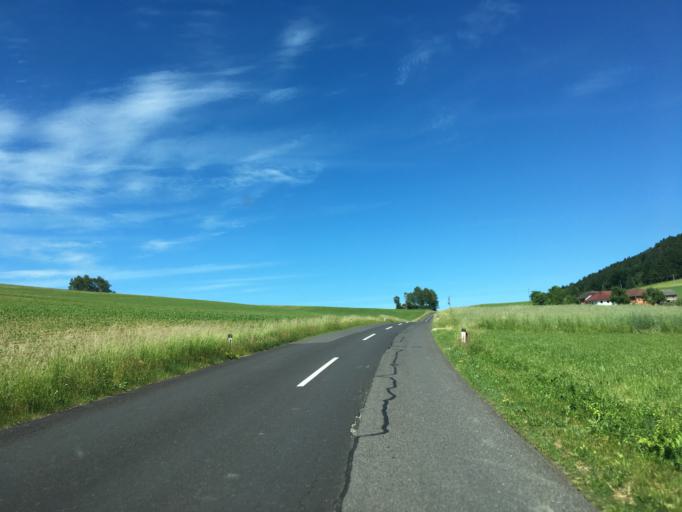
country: AT
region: Upper Austria
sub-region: Politischer Bezirk Urfahr-Umgebung
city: Eidenberg
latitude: 48.4116
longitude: 14.2174
